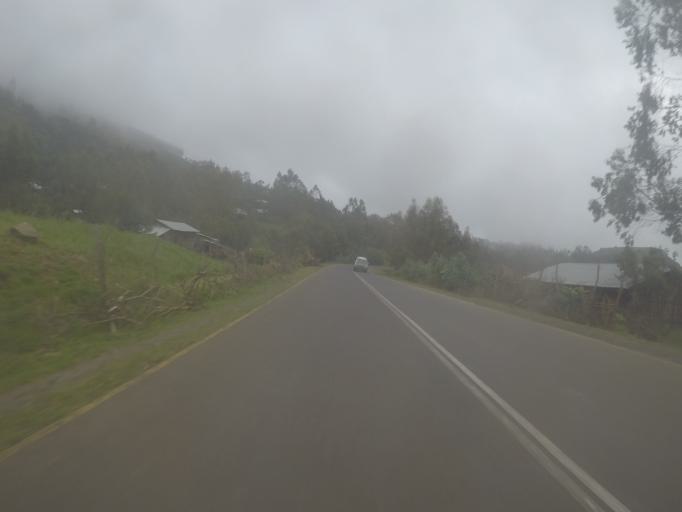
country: ET
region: Amhara
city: Gondar
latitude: 12.7379
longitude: 37.5155
